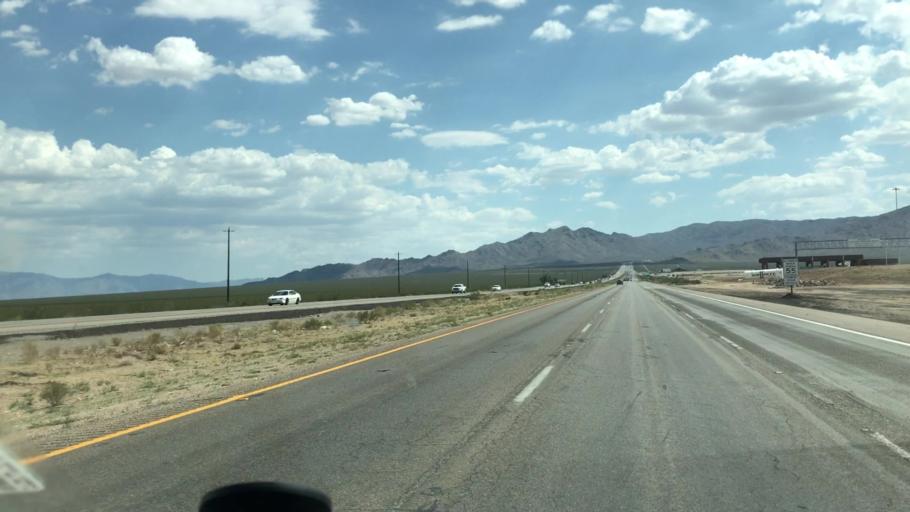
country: US
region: Nevada
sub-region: Clark County
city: Sandy Valley
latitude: 35.5193
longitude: -115.4291
